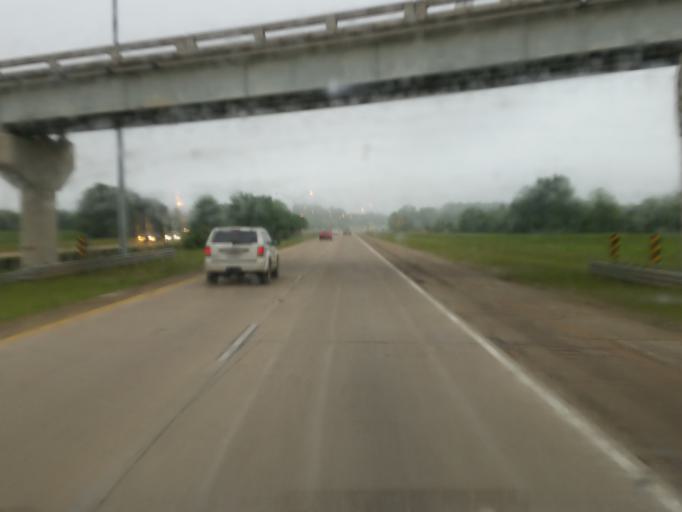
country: US
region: Louisiana
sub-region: Bossier Parish
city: Red Chute
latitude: 32.5400
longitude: -93.6282
